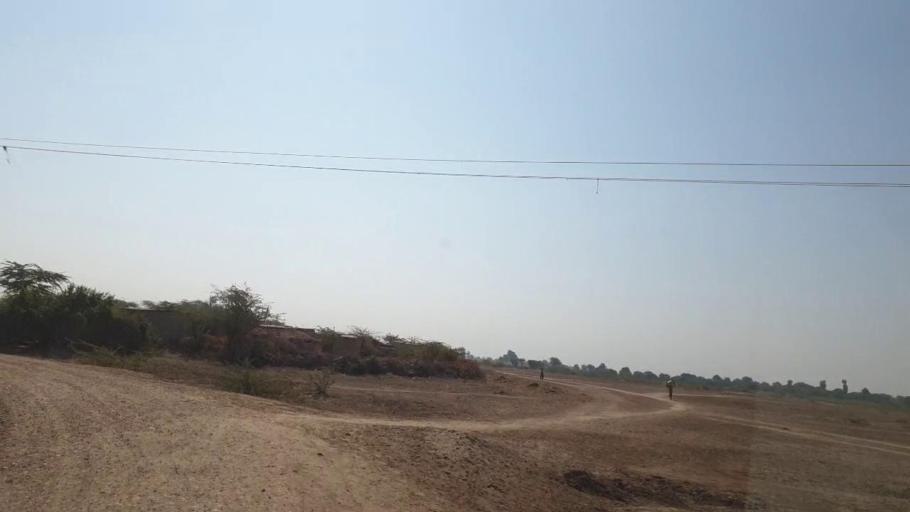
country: PK
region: Sindh
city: Kunri
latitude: 25.1682
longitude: 69.5303
